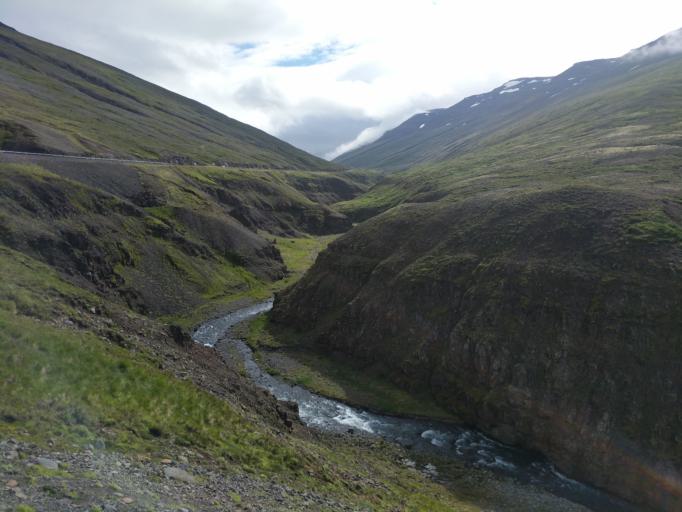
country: IS
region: Northeast
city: Dalvik
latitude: 65.4633
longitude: -18.8680
